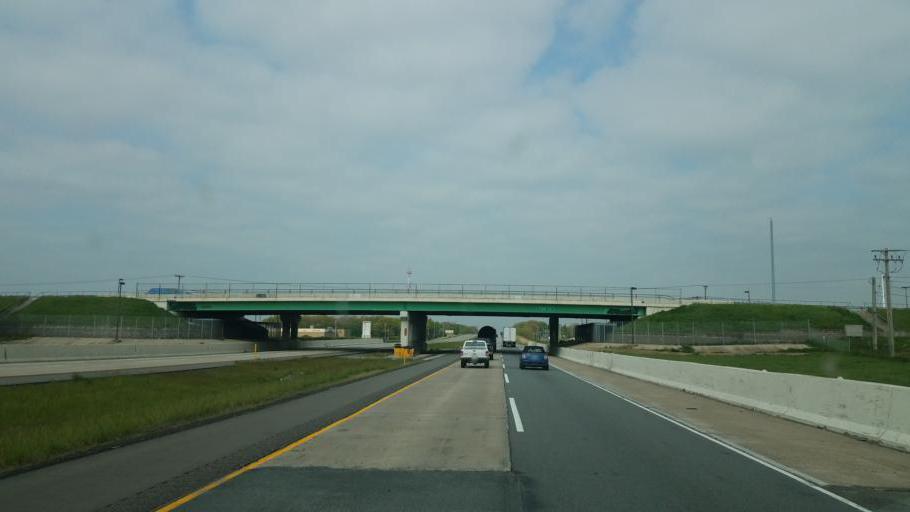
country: US
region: Indiana
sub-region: Saint Joseph County
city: Georgetown
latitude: 41.7164
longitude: -86.1862
